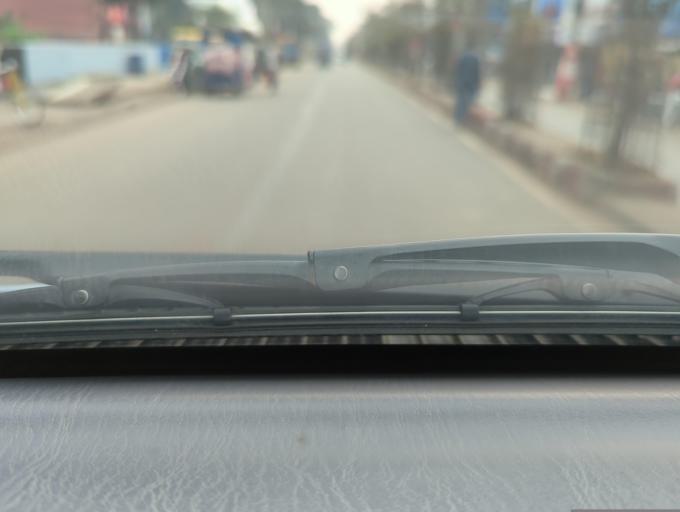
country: BD
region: Sylhet
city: Maulavi Bazar
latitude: 24.4834
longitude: 91.7655
